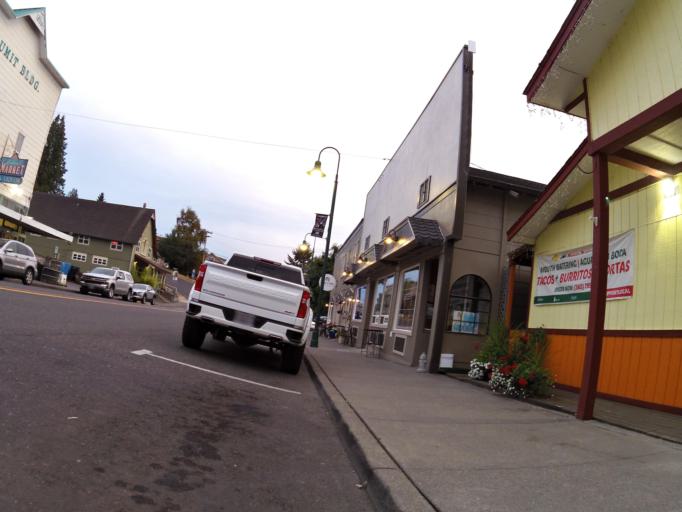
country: US
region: Washington
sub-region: Wahkiakum County
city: Cathlamet
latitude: 46.2023
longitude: -123.3852
